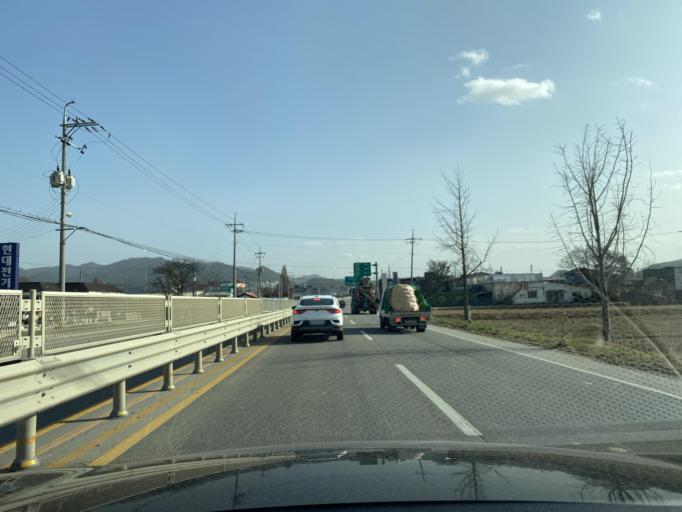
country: KR
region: Chungcheongnam-do
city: Yesan
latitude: 36.6849
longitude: 126.8138
